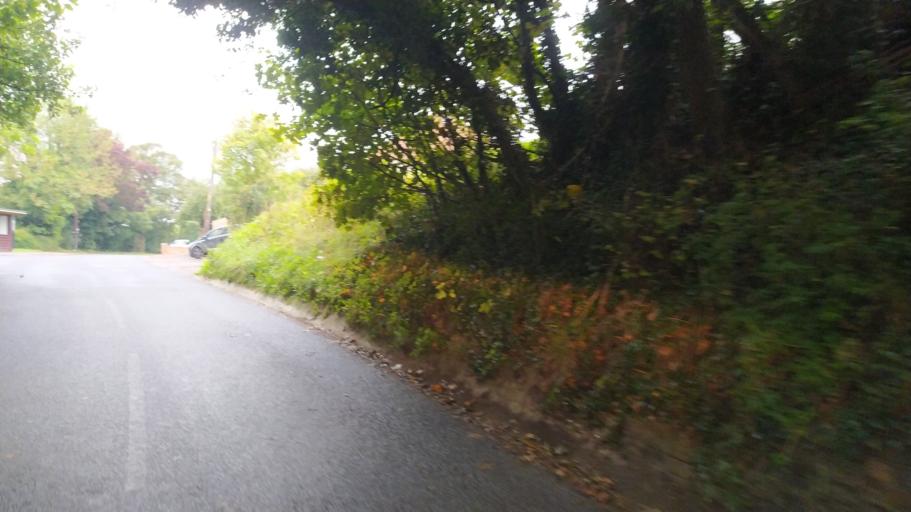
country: GB
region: England
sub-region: Wiltshire
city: Allington
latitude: 51.1200
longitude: -1.7336
